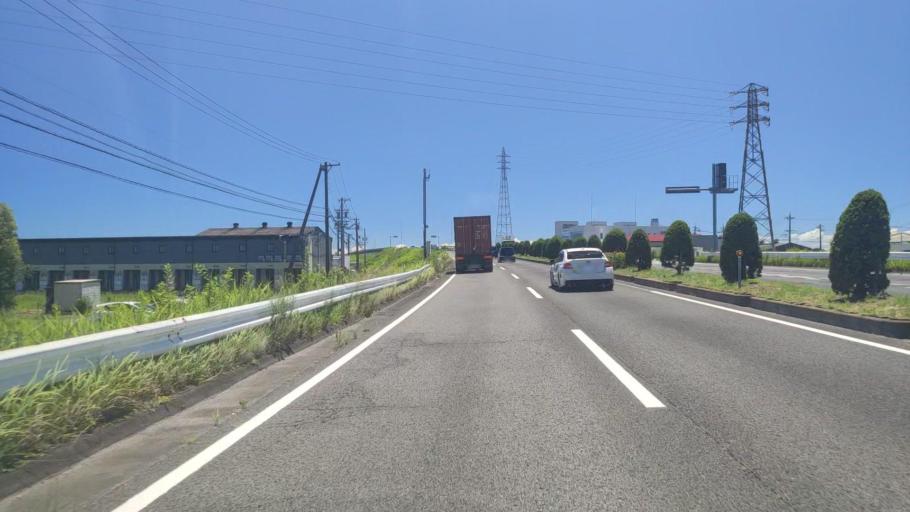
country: JP
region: Mie
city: Suzuka
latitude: 34.9118
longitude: 136.6053
